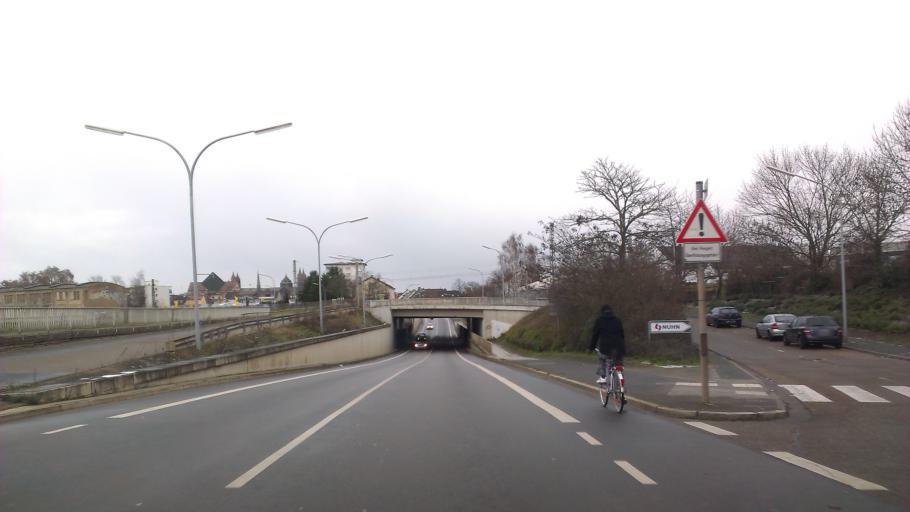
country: DE
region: Rheinland-Pfalz
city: Worms
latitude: 49.6217
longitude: 8.3534
